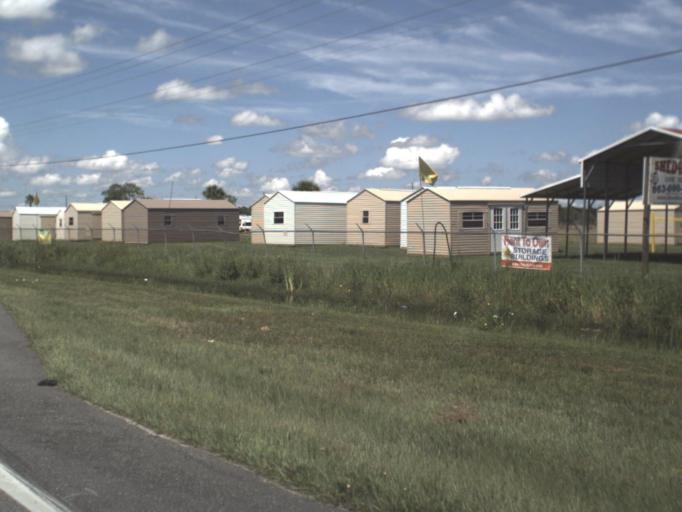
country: US
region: Florida
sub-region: Polk County
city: Fussels Corner
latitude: 28.0564
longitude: -81.8247
